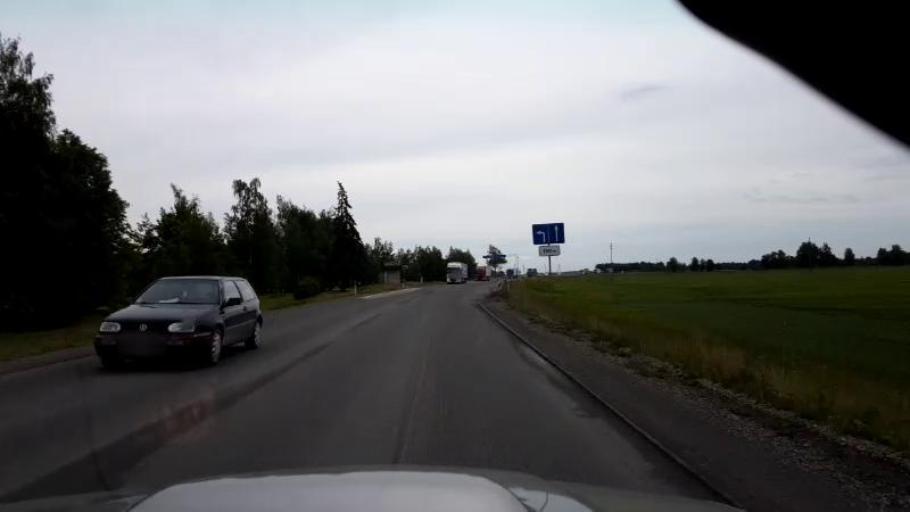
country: LV
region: Bauskas Rajons
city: Bauska
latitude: 56.3094
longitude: 24.3379
